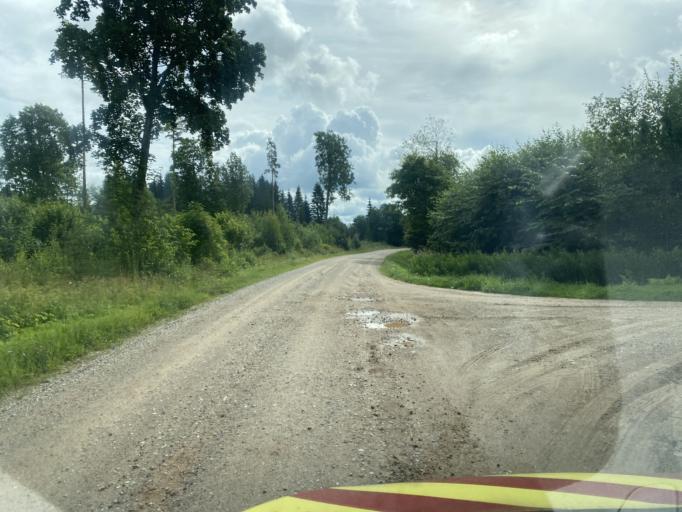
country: EE
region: Viljandimaa
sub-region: Karksi vald
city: Karksi-Nuia
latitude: 58.0603
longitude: 25.5371
